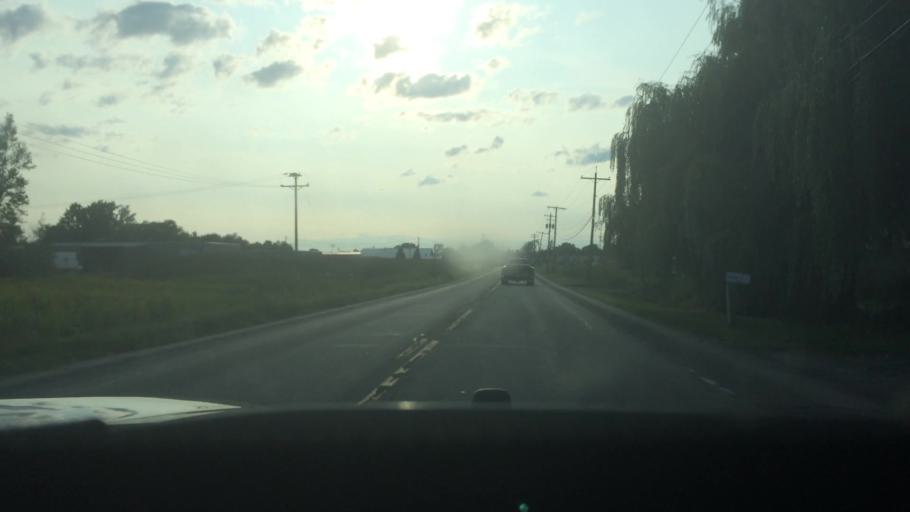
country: US
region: New York
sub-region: St. Lawrence County
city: Ogdensburg
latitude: 44.6893
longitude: -75.4699
